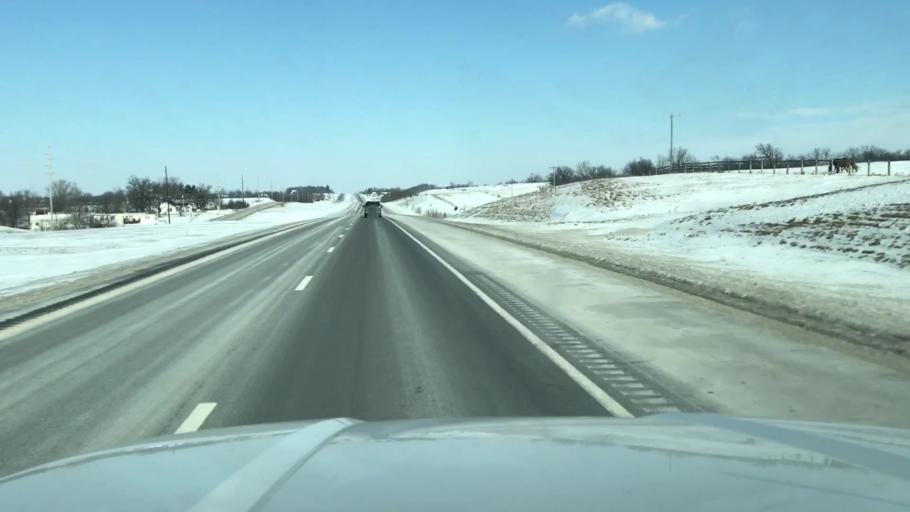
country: US
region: Missouri
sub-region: Nodaway County
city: Maryville
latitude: 40.1867
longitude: -94.8678
